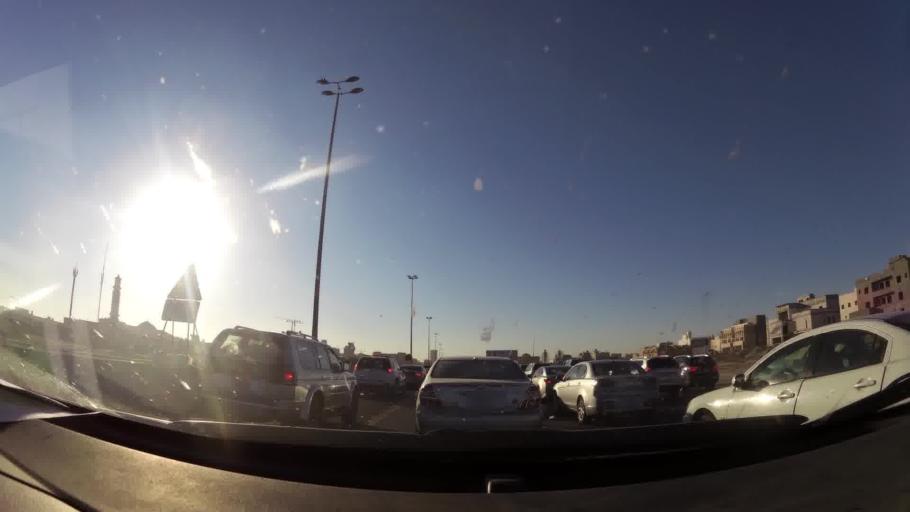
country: KW
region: Al Ahmadi
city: Al Fintas
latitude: 29.1907
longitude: 48.1100
